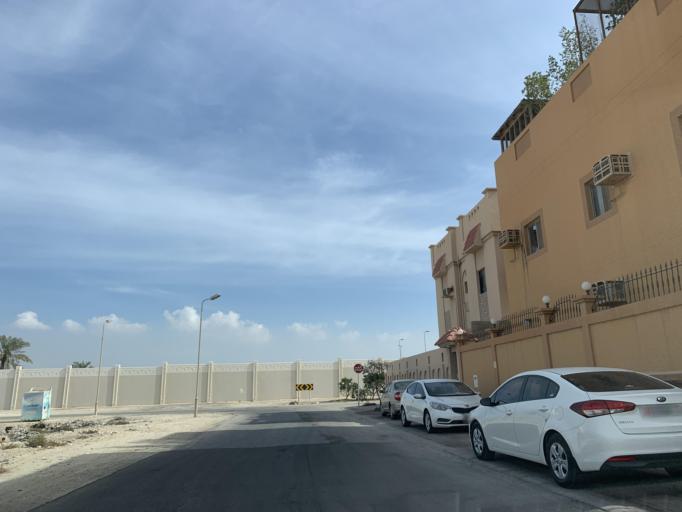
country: BH
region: Central Governorate
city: Madinat Hamad
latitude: 26.1311
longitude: 50.4777
